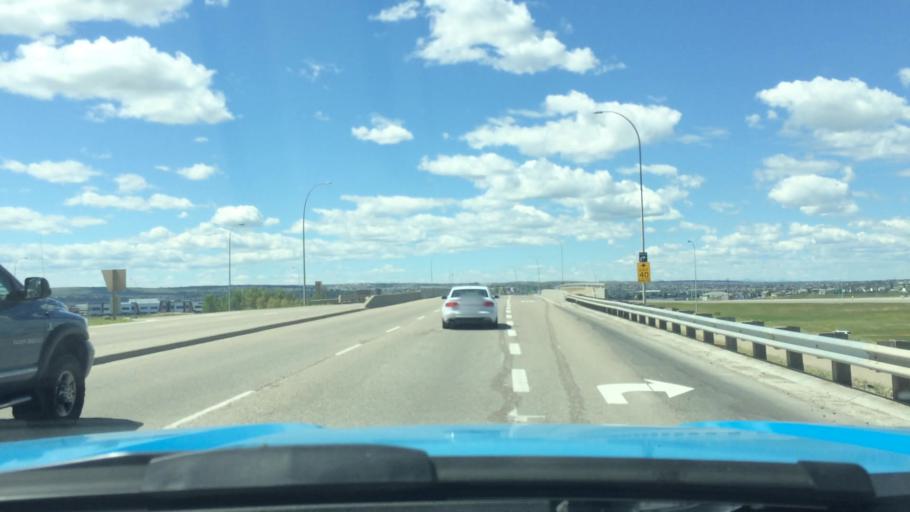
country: CA
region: Alberta
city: Calgary
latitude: 51.1543
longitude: -114.0156
